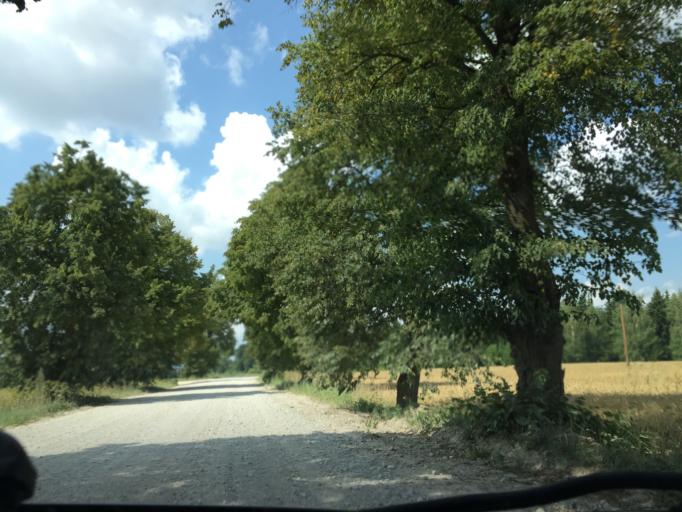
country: LT
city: Zagare
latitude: 56.4034
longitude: 23.2428
